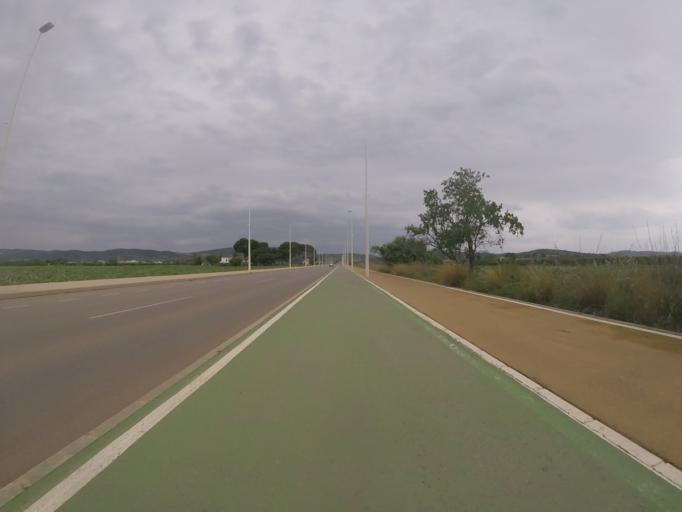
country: ES
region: Valencia
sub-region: Provincia de Castello
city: Torreblanca
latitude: 40.2202
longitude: 0.2163
